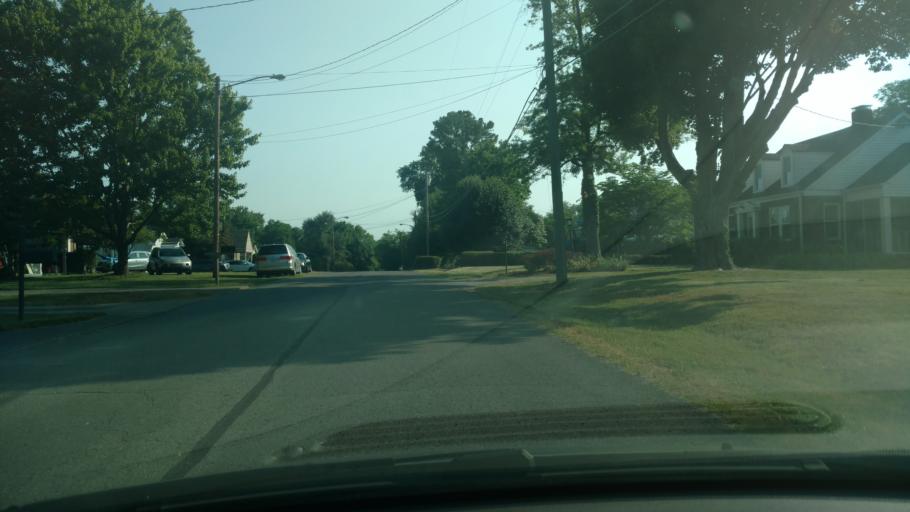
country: US
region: Tennessee
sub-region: Davidson County
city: Lakewood
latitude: 36.2121
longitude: -86.7104
